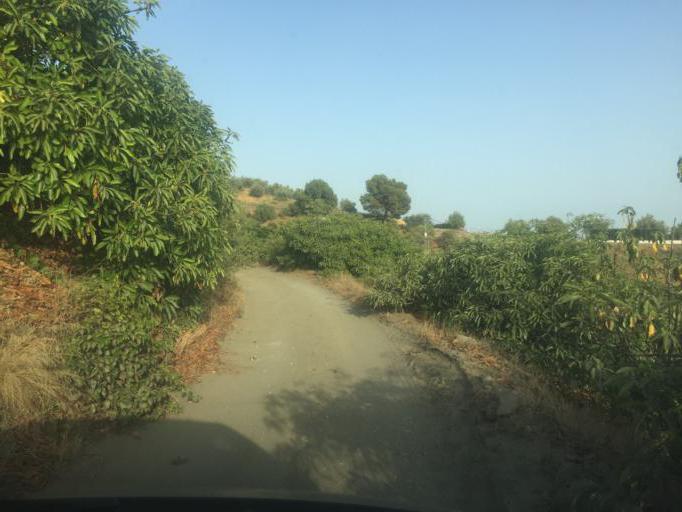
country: ES
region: Andalusia
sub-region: Provincia de Malaga
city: Frigiliana
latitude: 36.8056
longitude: -3.9257
